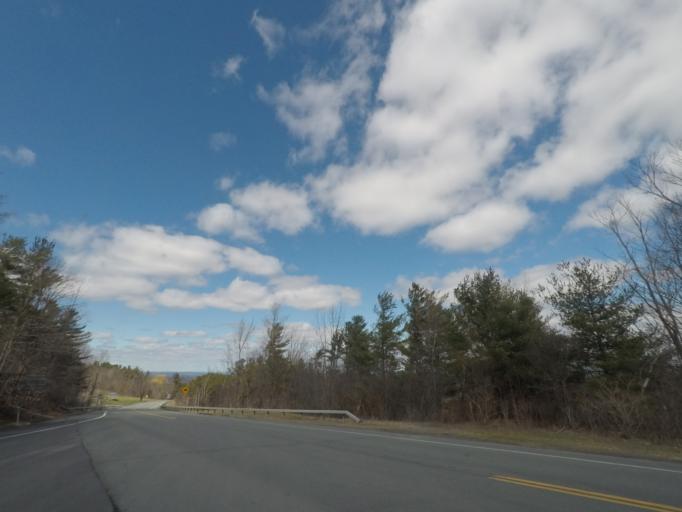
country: US
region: New York
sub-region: Albany County
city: Voorheesville
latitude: 42.6159
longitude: -73.9753
